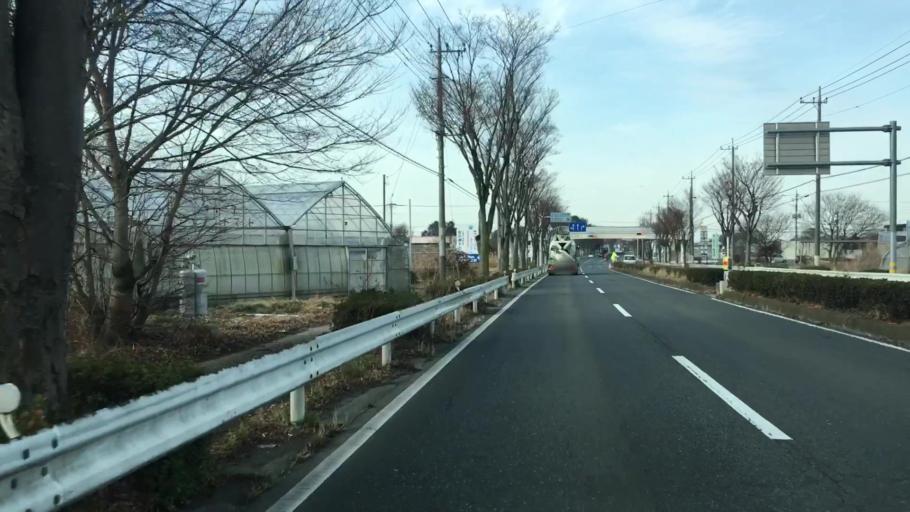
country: JP
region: Gunma
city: Tatebayashi
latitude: 36.2300
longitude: 139.5637
